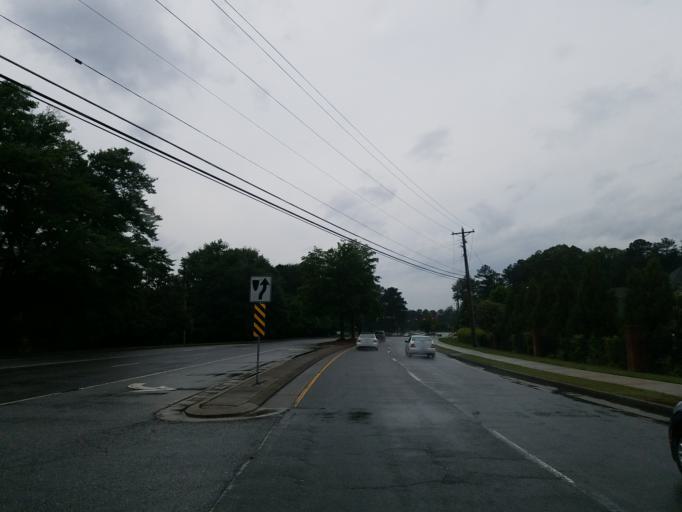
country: US
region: Georgia
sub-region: Cobb County
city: Kennesaw
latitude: 34.0344
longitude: -84.5524
